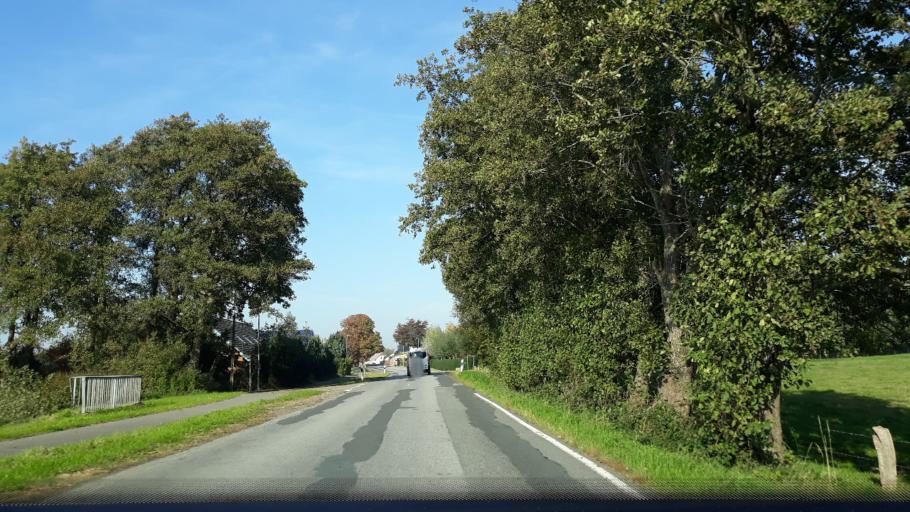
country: DE
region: Schleswig-Holstein
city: Borm
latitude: 54.4015
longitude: 9.3791
